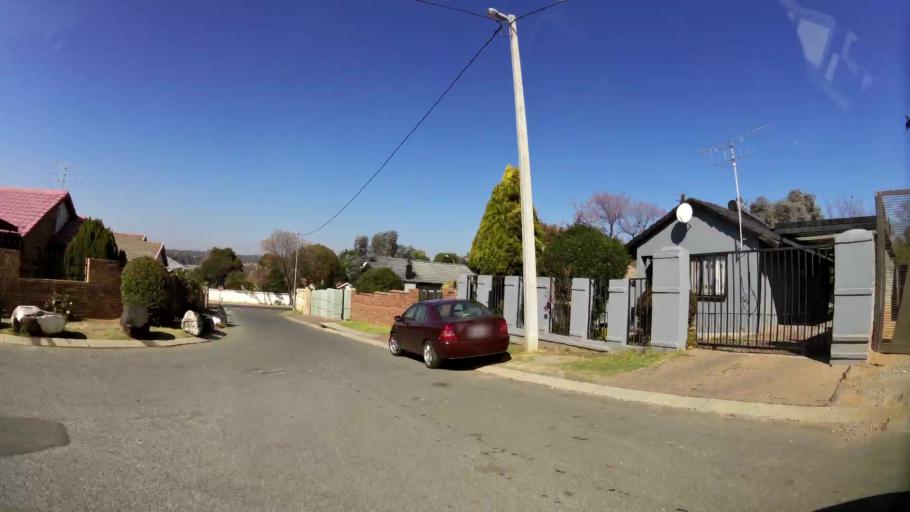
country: ZA
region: Gauteng
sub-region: City of Johannesburg Metropolitan Municipality
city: Modderfontein
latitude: -26.1189
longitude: 28.1027
